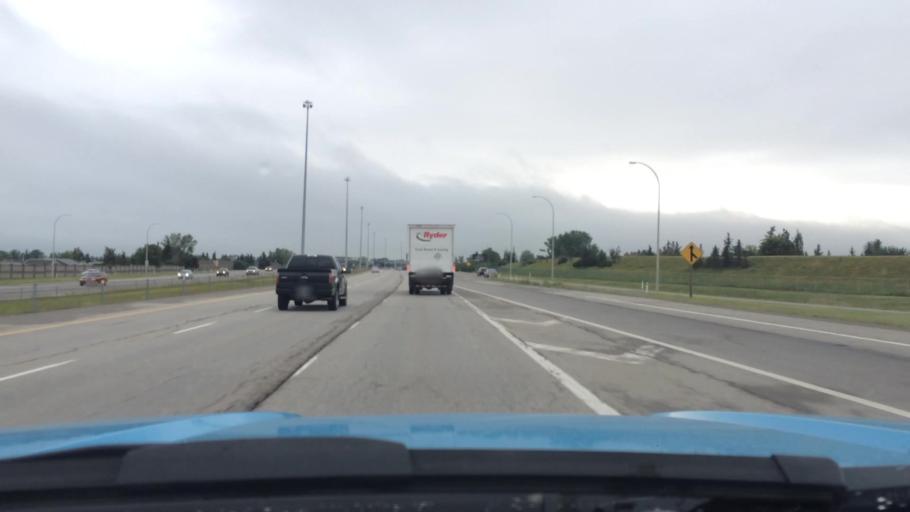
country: CA
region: Alberta
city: Airdrie
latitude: 51.2722
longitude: -114.0012
